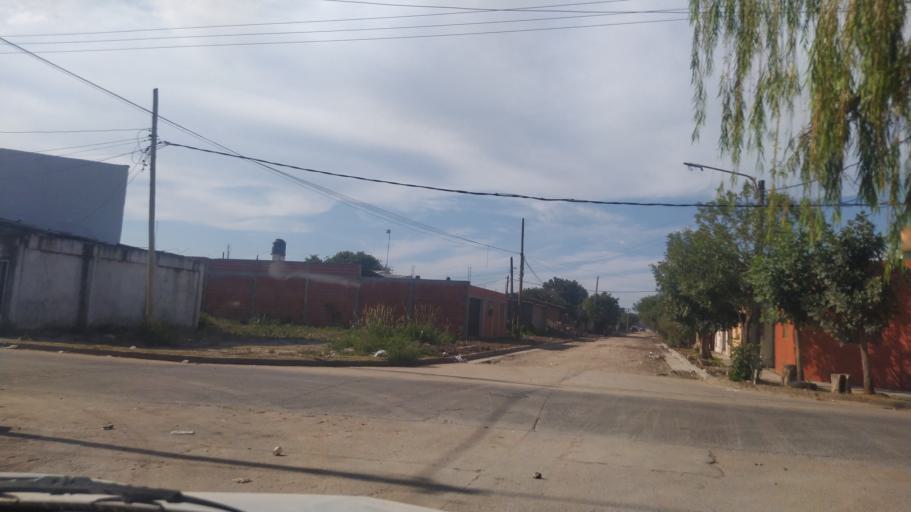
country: AR
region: Corrientes
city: Corrientes
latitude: -27.4907
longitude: -58.8119
